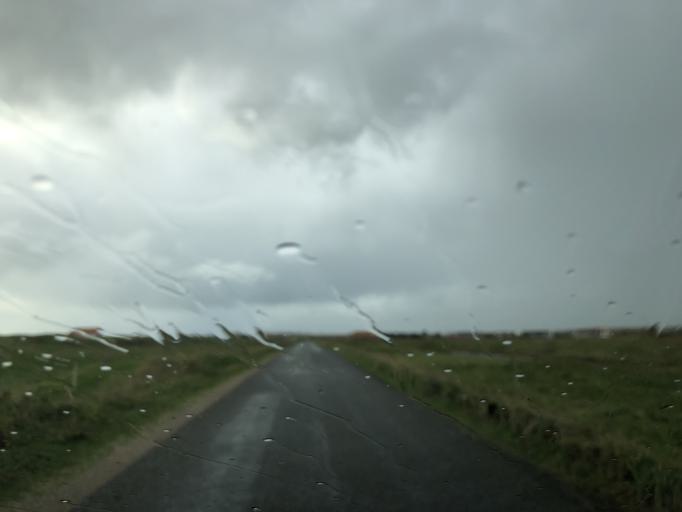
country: DK
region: Central Jutland
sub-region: Lemvig Kommune
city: Harboore
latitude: 56.5403
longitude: 8.1347
